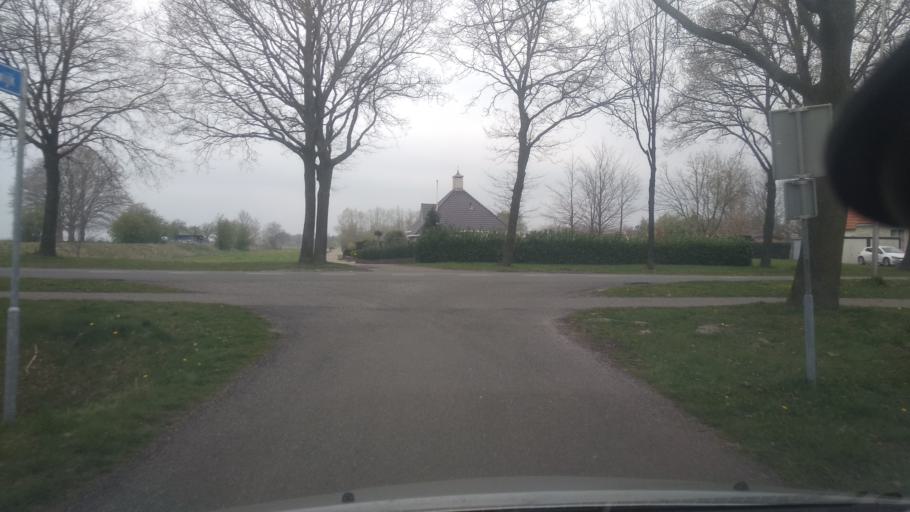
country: NL
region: Groningen
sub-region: Gemeente Stadskanaal
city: Stadskanaal
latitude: 52.9496
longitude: 6.9881
